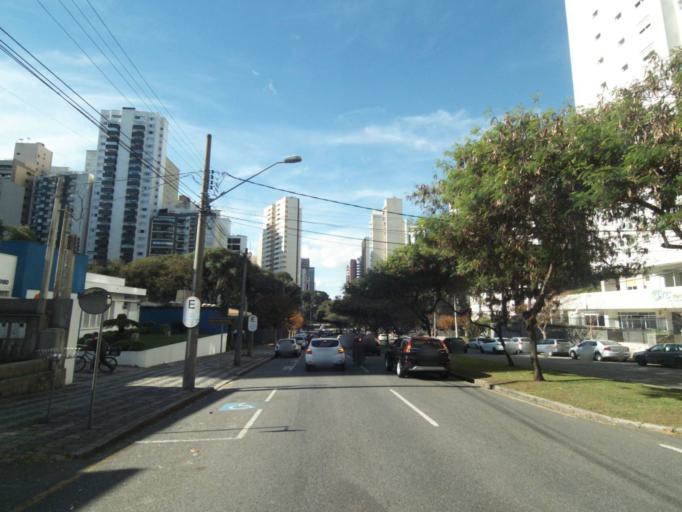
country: BR
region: Parana
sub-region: Curitiba
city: Curitiba
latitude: -25.4484
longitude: -49.2908
